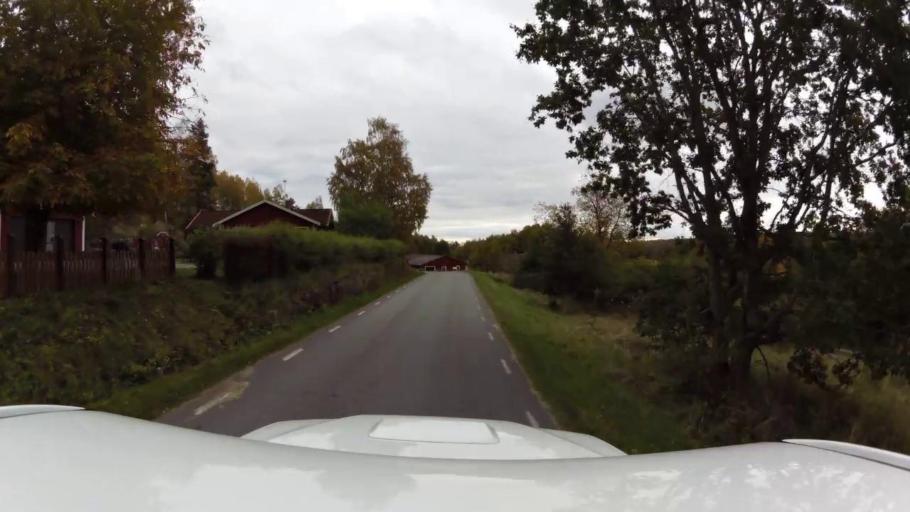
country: SE
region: OEstergoetland
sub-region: Linkopings Kommun
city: Ljungsbro
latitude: 58.5247
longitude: 15.4755
